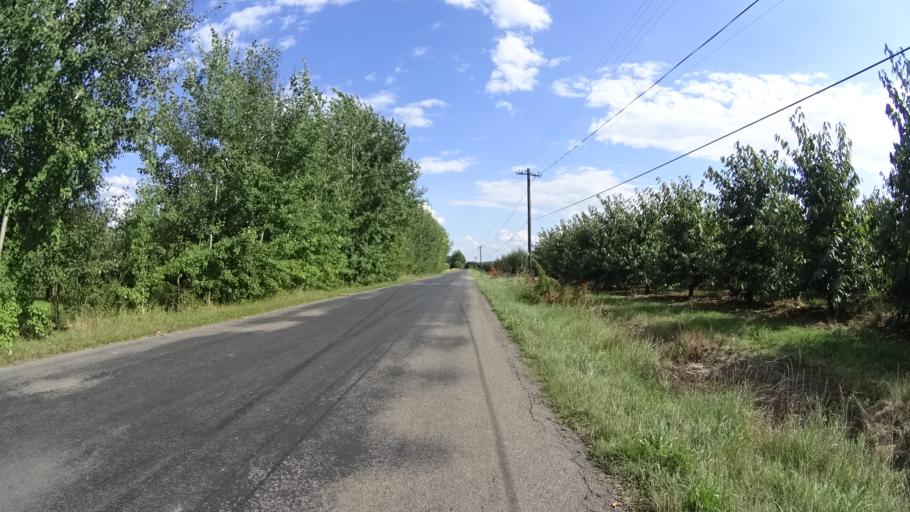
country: PL
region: Masovian Voivodeship
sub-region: Powiat grojecki
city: Mogielnica
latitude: 51.6892
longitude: 20.7497
